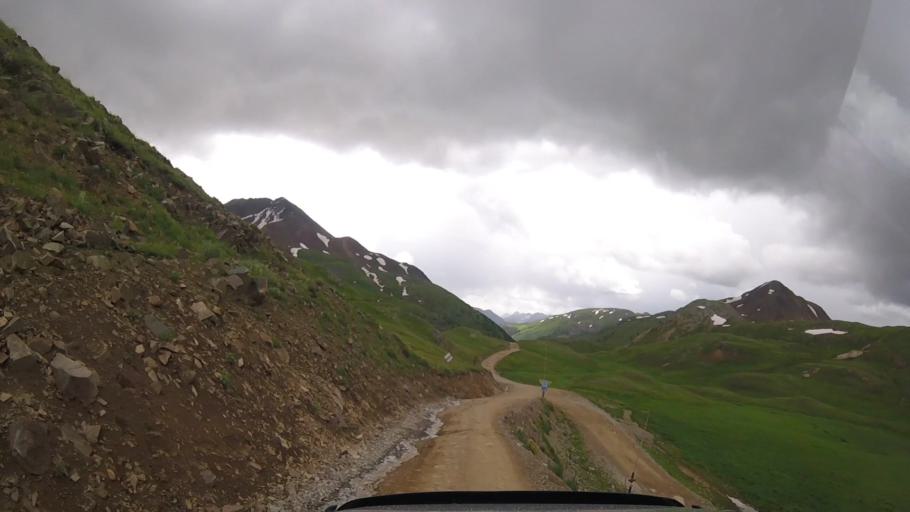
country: US
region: Colorado
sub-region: Ouray County
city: Ouray
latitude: 37.9578
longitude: -107.5755
